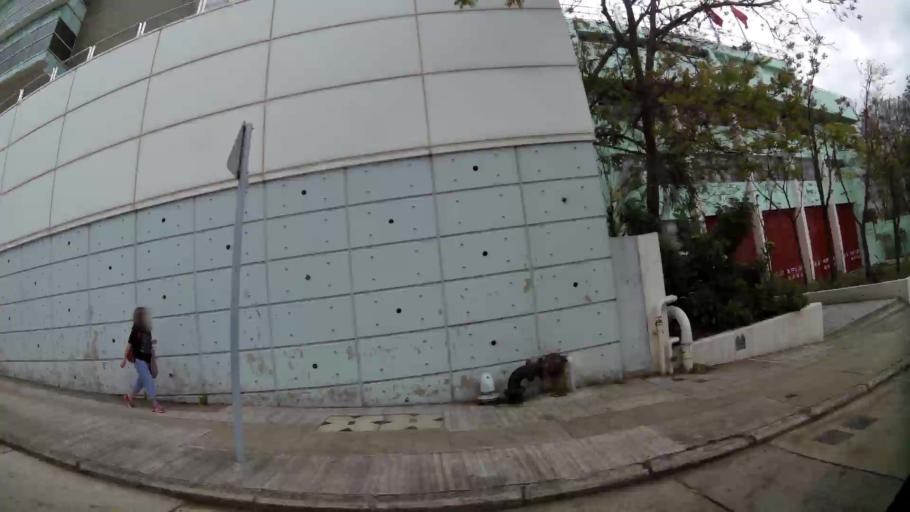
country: HK
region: Sham Shui Po
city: Sham Shui Po
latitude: 22.3388
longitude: 114.1667
